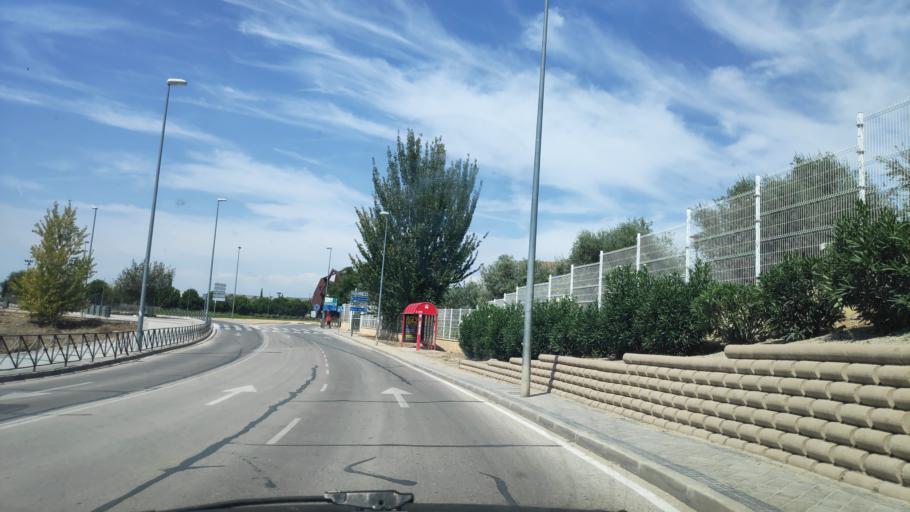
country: ES
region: Madrid
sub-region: Provincia de Madrid
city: Arganda
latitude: 40.3058
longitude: -3.4462
